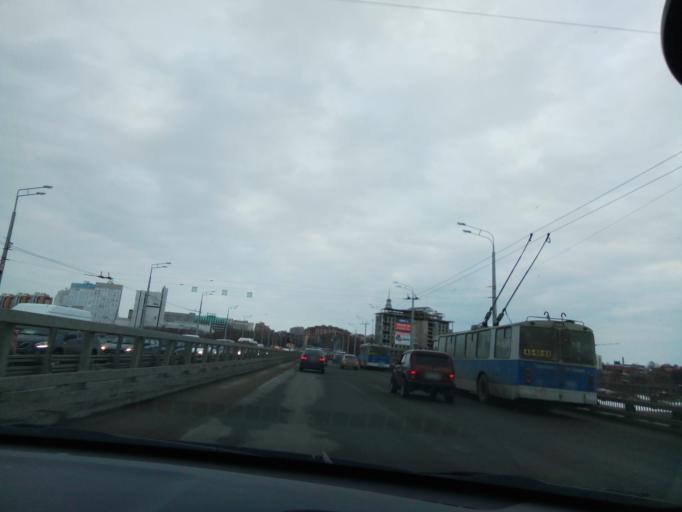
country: RU
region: Chuvashia
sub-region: Cheboksarskiy Rayon
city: Cheboksary
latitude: 56.1442
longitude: 47.2458
